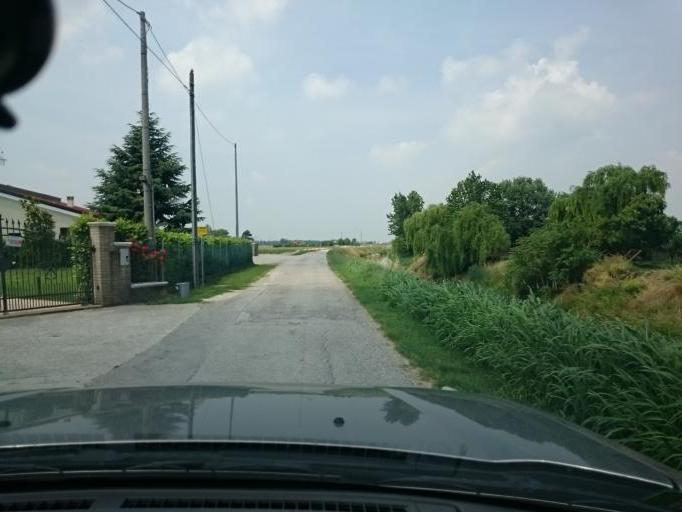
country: IT
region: Veneto
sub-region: Provincia di Padova
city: Codevigo
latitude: 45.2481
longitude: 12.0955
